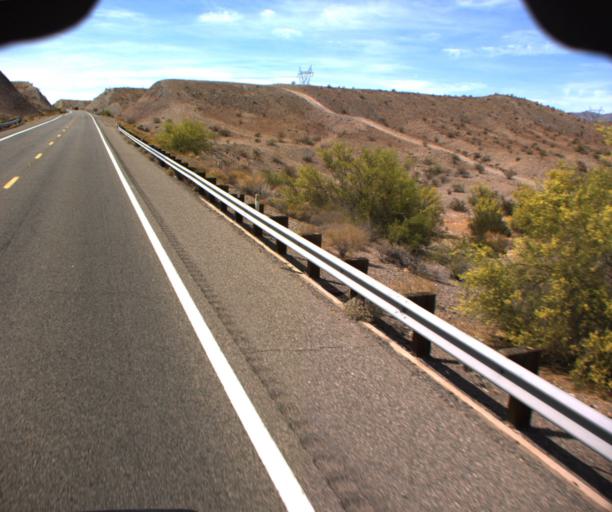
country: US
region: Arizona
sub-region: Mohave County
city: Lake Havasu City
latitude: 34.4240
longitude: -114.2049
